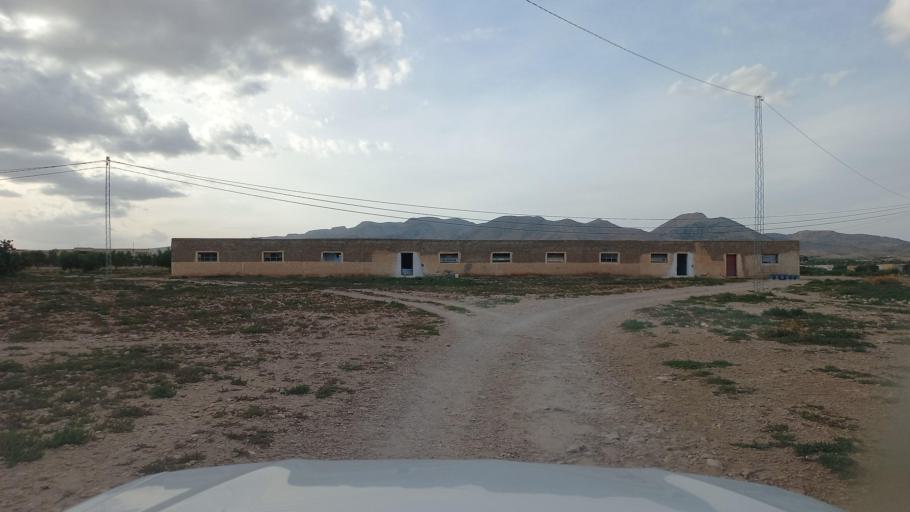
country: TN
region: Al Qasrayn
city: Sbiba
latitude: 35.4365
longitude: 9.0947
